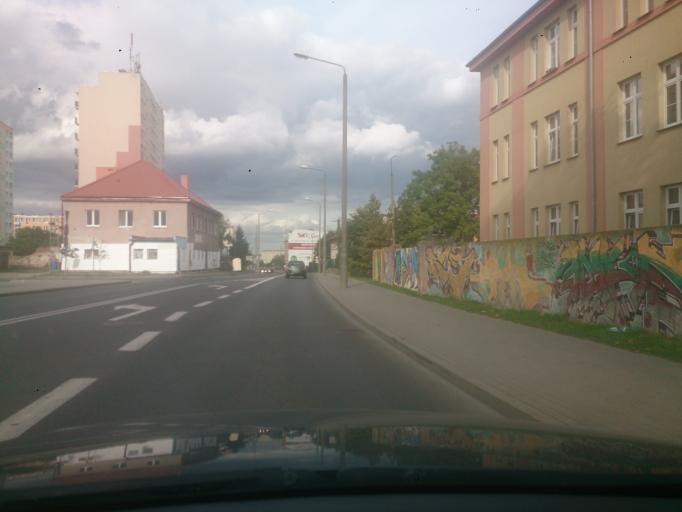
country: PL
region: Kujawsko-Pomorskie
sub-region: Grudziadz
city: Grudziadz
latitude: 53.4740
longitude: 18.7394
